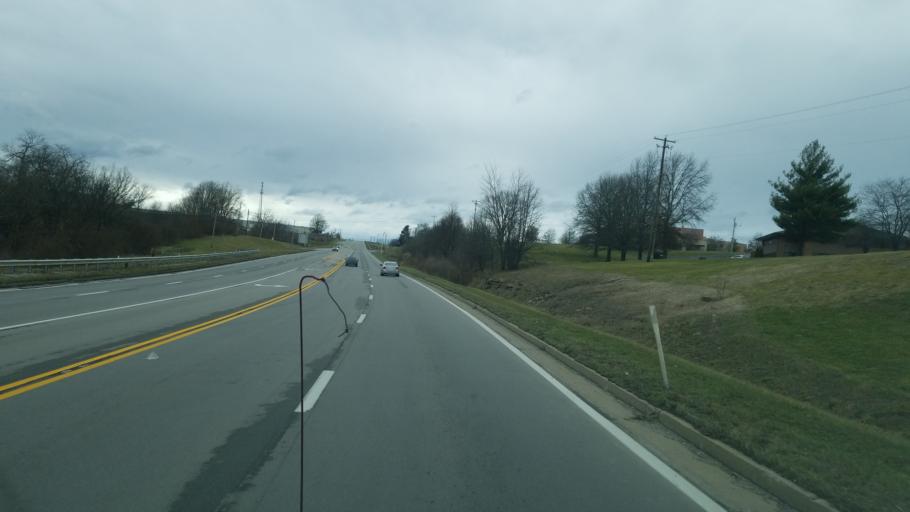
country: US
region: Ohio
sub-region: Brown County
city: Aberdeen
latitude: 38.6371
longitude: -83.8038
